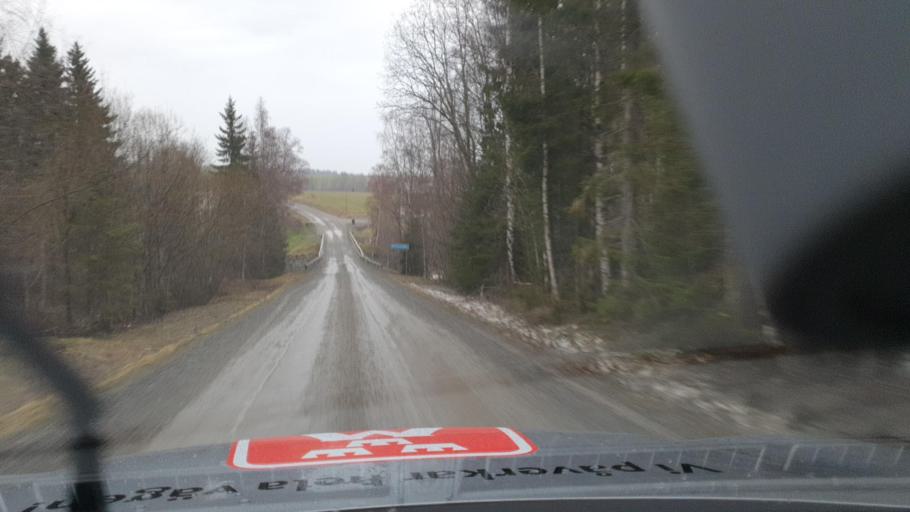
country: SE
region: Vaesternorrland
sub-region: OErnskoeldsviks Kommun
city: Bjasta
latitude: 63.2413
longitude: 18.4047
